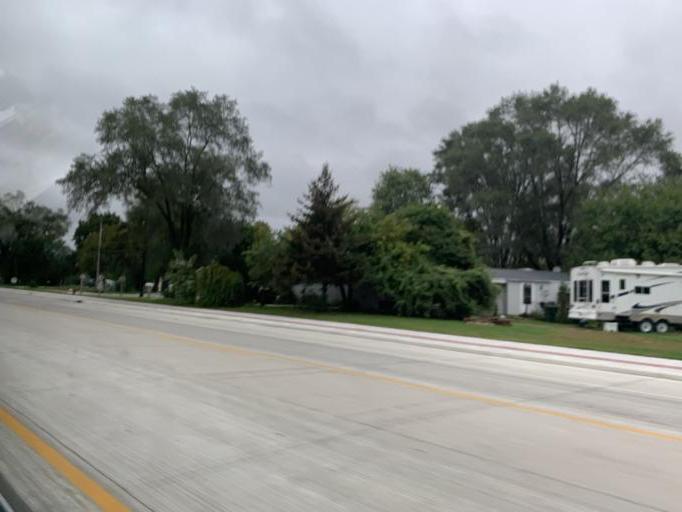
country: US
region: Wisconsin
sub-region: Crawford County
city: Prairie du Chien
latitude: 43.0327
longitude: -91.1345
